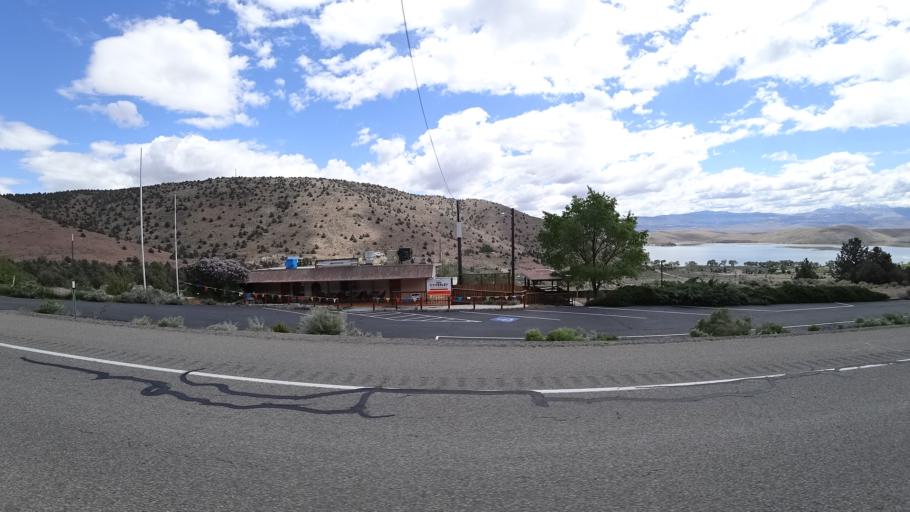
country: US
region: Nevada
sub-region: Lyon County
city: Smith Valley
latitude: 38.7028
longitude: -119.5521
